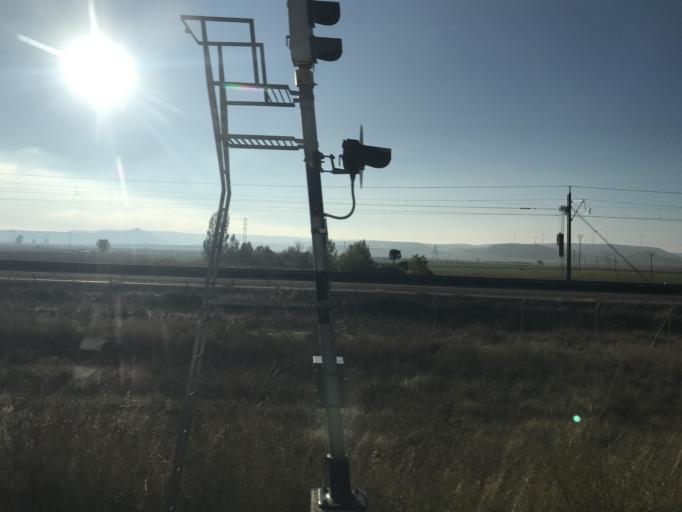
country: ES
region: Castille and Leon
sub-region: Provincia de Palencia
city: Quintana del Puente
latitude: 42.0752
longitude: -4.2060
